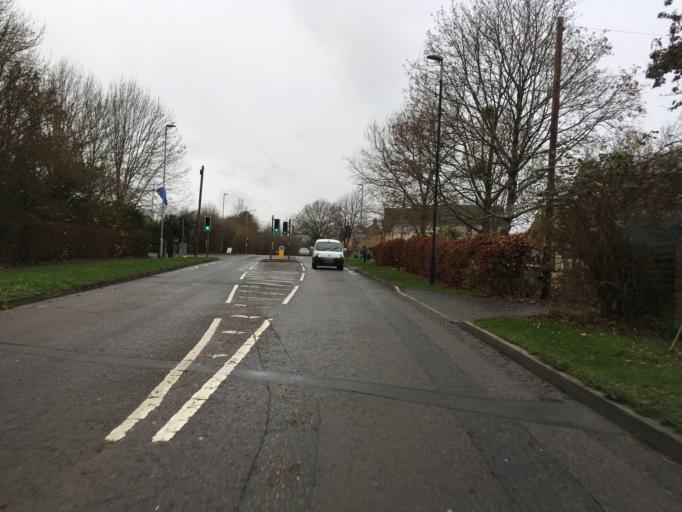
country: GB
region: England
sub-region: Wiltshire
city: Malmesbury
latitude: 51.5950
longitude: -2.1021
